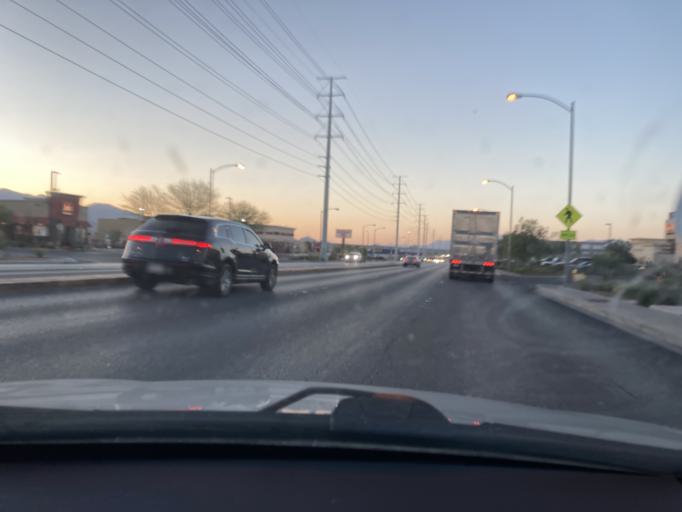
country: US
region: Nevada
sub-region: Clark County
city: Enterprise
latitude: 36.0594
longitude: -115.2792
